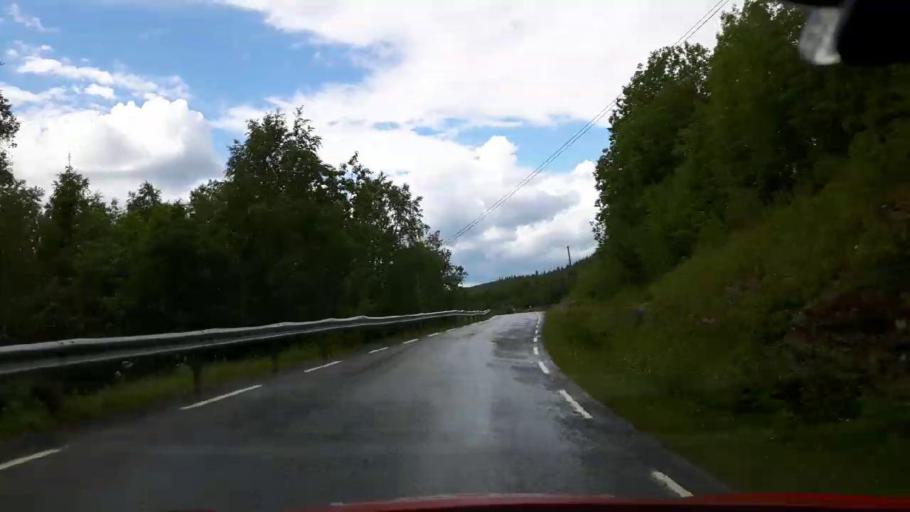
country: NO
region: Nord-Trondelag
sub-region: Lierne
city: Sandvika
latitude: 64.1074
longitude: 13.9842
